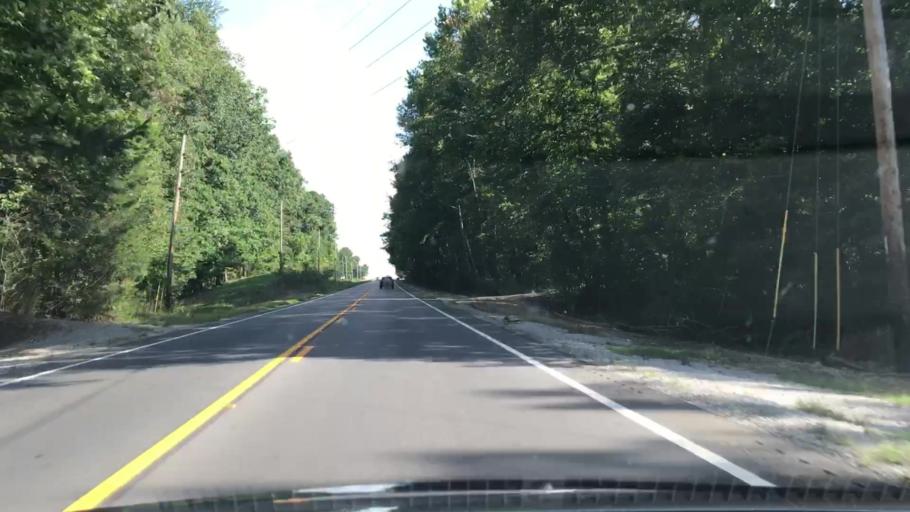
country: US
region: Alabama
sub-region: Madison County
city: Harvest
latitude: 34.9183
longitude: -86.7632
